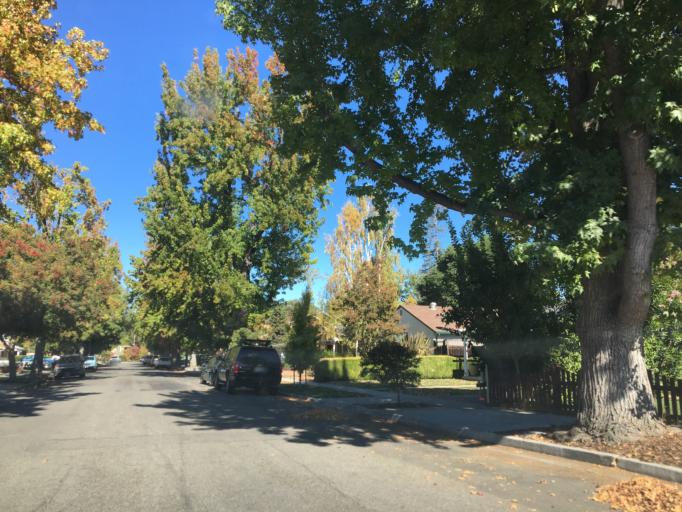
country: US
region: California
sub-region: Santa Clara County
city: Buena Vista
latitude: 37.3018
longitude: -121.8825
